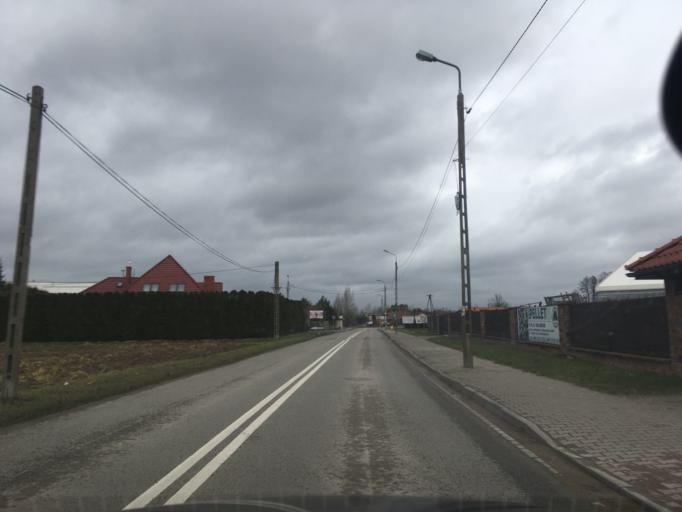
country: PL
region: Masovian Voivodeship
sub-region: Powiat piaseczynski
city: Lesznowola
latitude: 52.1209
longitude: 20.9466
